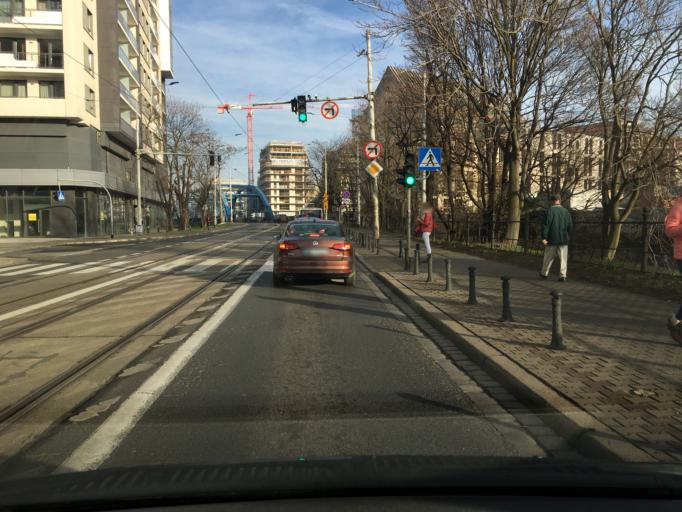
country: PL
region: Lower Silesian Voivodeship
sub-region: Powiat wroclawski
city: Wroclaw
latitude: 51.1129
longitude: 17.0233
